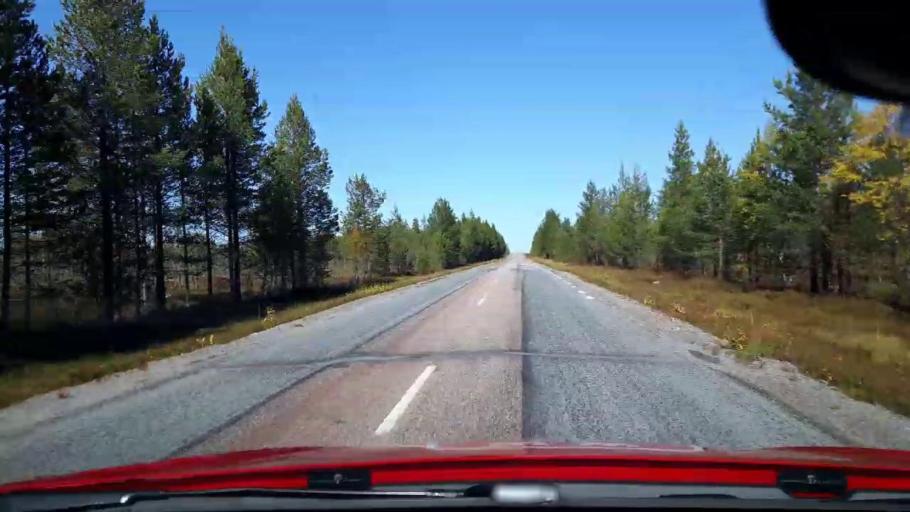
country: SE
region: Jaemtland
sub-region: Harjedalens Kommun
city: Sveg
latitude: 61.7243
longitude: 14.1668
